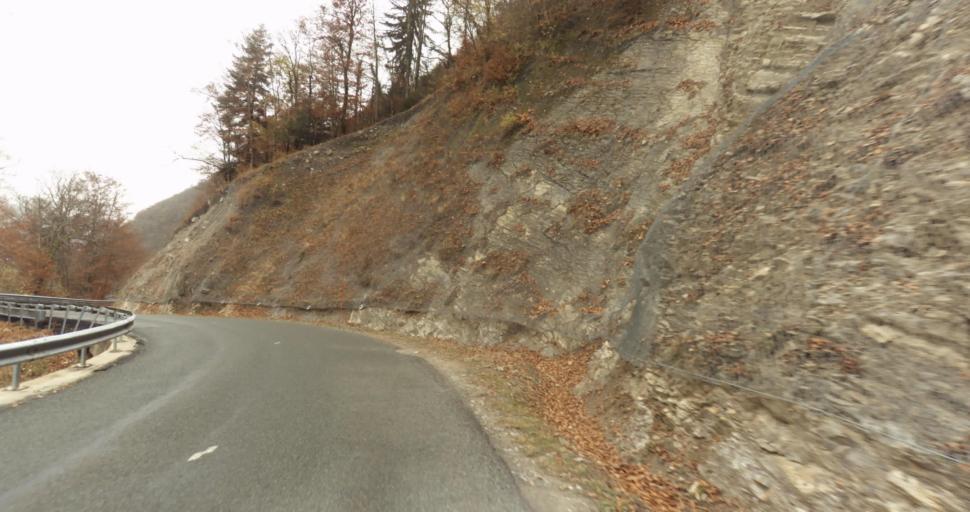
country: FR
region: Rhone-Alpes
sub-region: Departement de la Haute-Savoie
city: Doussard
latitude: 45.7856
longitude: 6.2591
